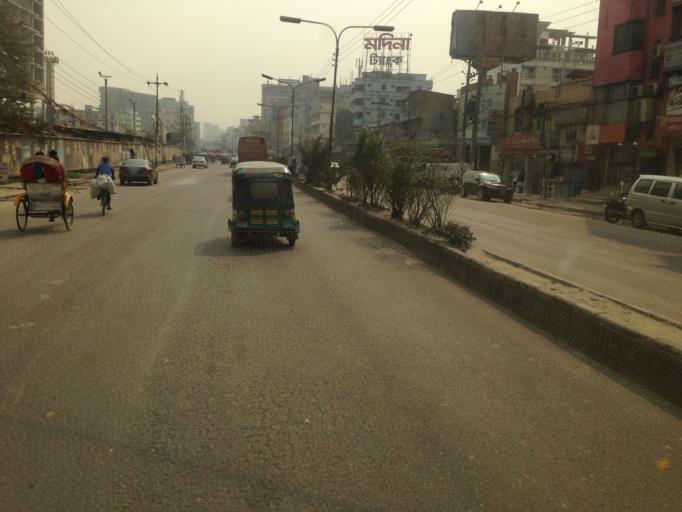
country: BD
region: Dhaka
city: Paltan
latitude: 23.8147
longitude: 90.4212
